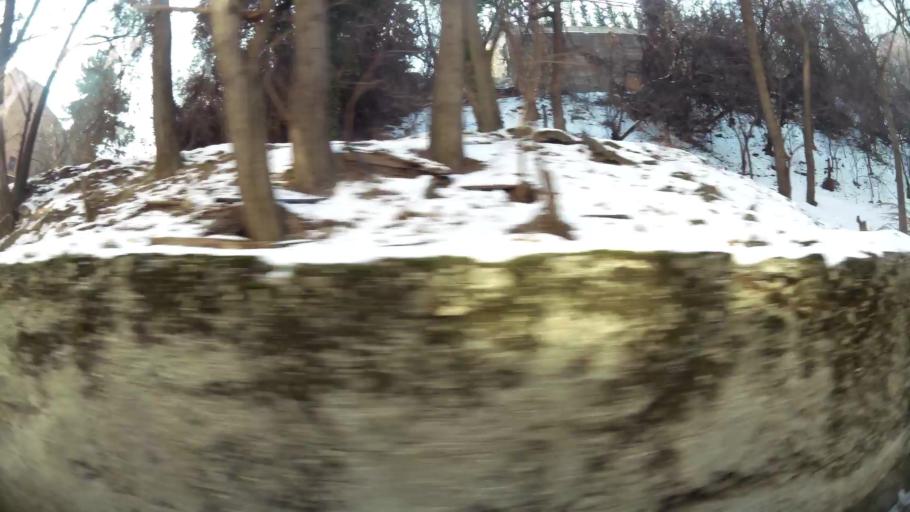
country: MK
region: Karpos
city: Skopje
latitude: 41.9865
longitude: 21.4268
